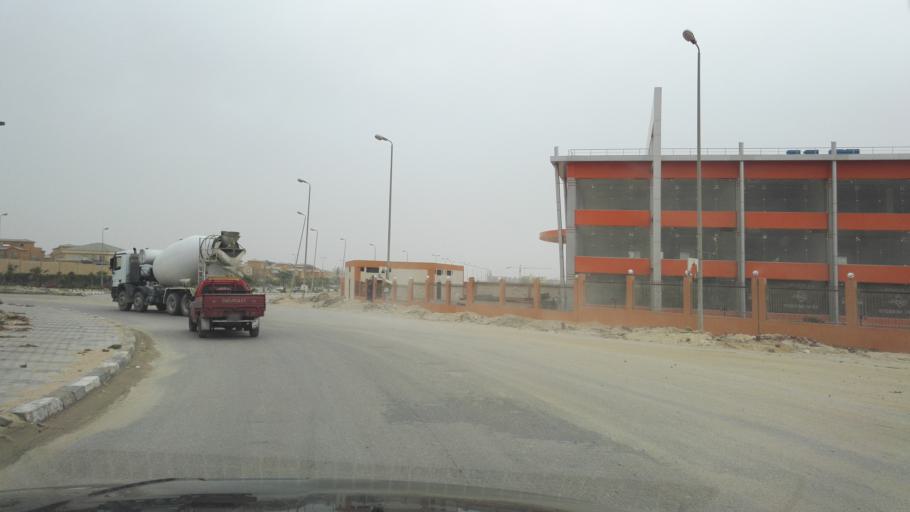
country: EG
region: Muhafazat al Qalyubiyah
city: Al Khankah
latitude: 30.0437
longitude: 31.5236
